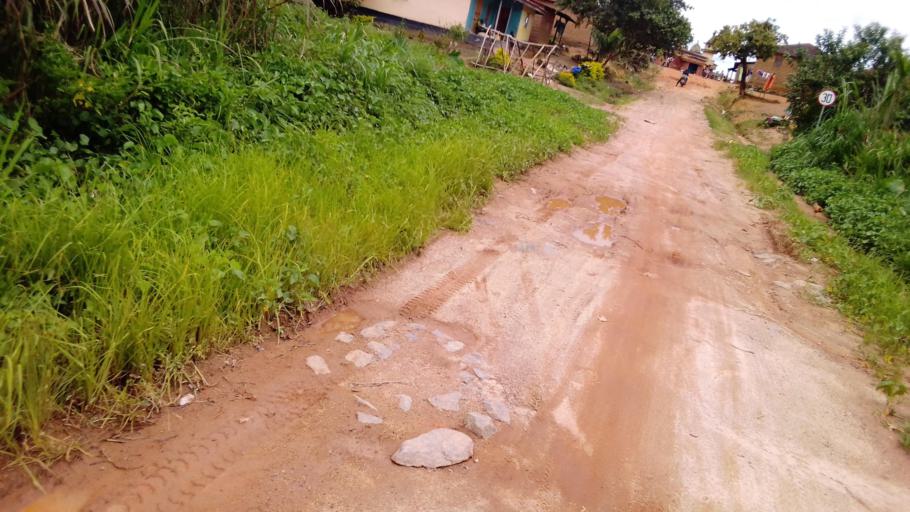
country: SL
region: Eastern Province
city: Koidu
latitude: 8.6871
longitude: -10.9292
